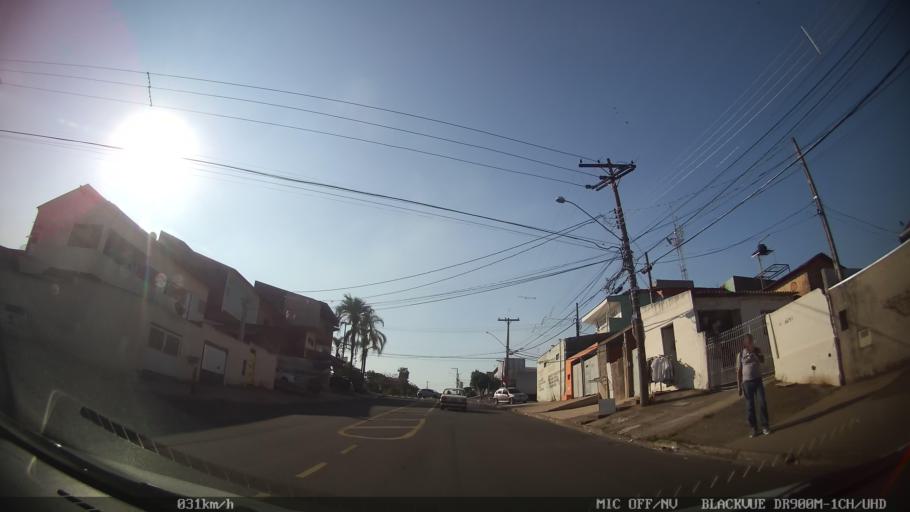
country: BR
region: Sao Paulo
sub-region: Campinas
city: Campinas
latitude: -22.9896
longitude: -47.1415
